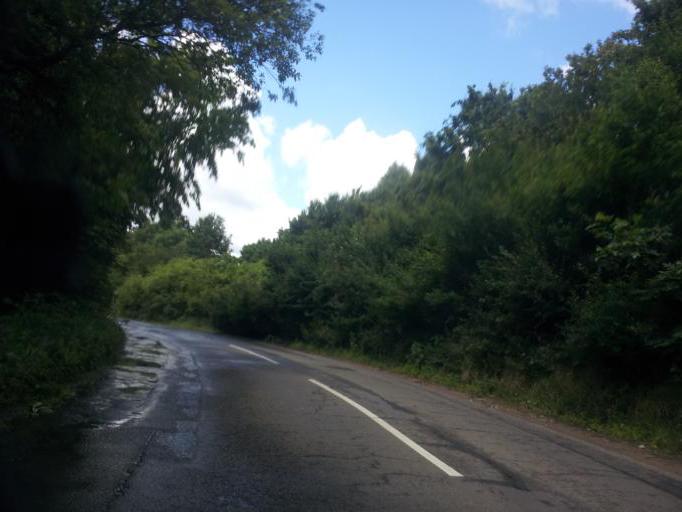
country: GB
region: England
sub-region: Kent
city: West Malling
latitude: 51.3114
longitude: 0.3654
